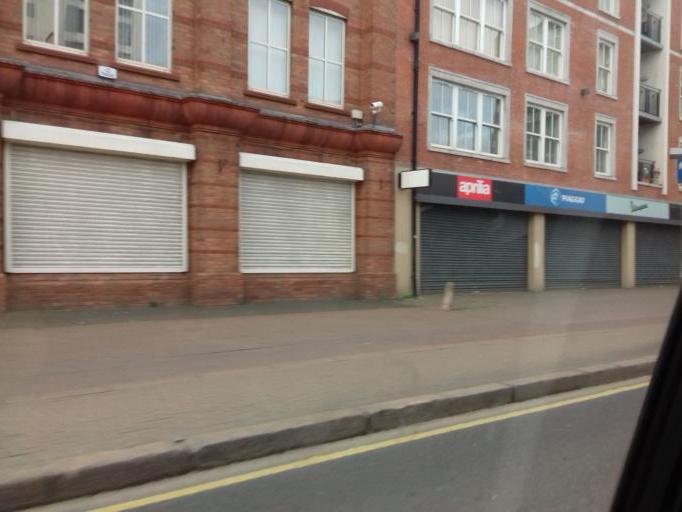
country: GB
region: Northern Ireland
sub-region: City of Belfast
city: Belfast
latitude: 54.5911
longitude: -5.9343
